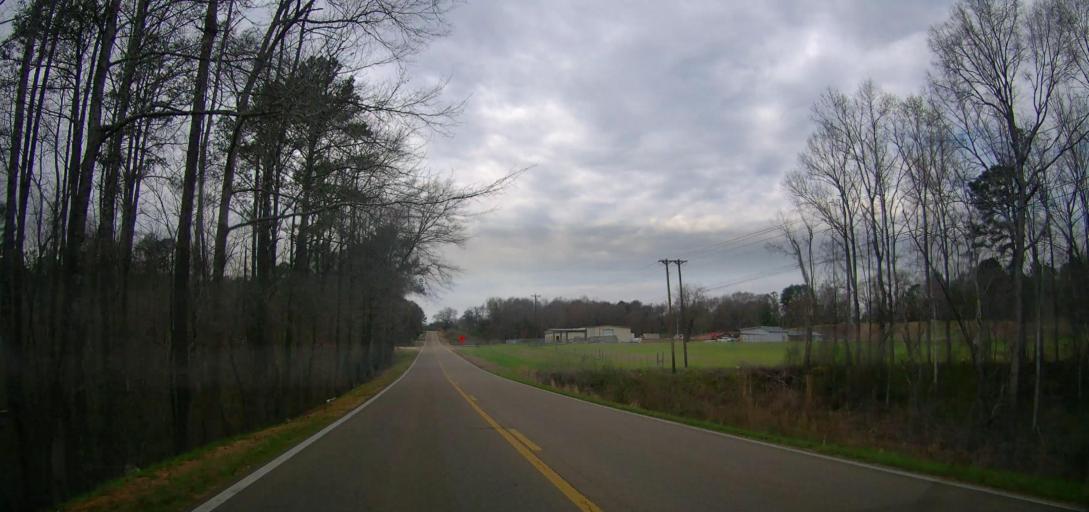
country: US
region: Mississippi
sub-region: Itawamba County
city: Fulton
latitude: 34.2772
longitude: -88.3623
